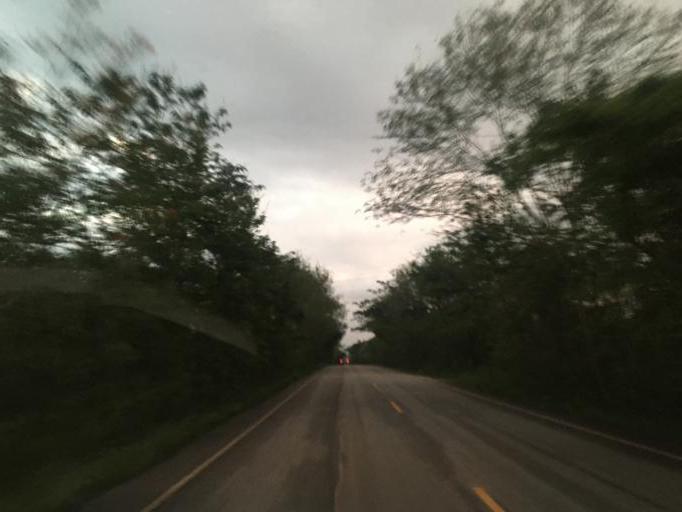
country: TH
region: Changwat Udon Thani
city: Udon Thani
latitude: 17.3166
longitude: 102.7118
